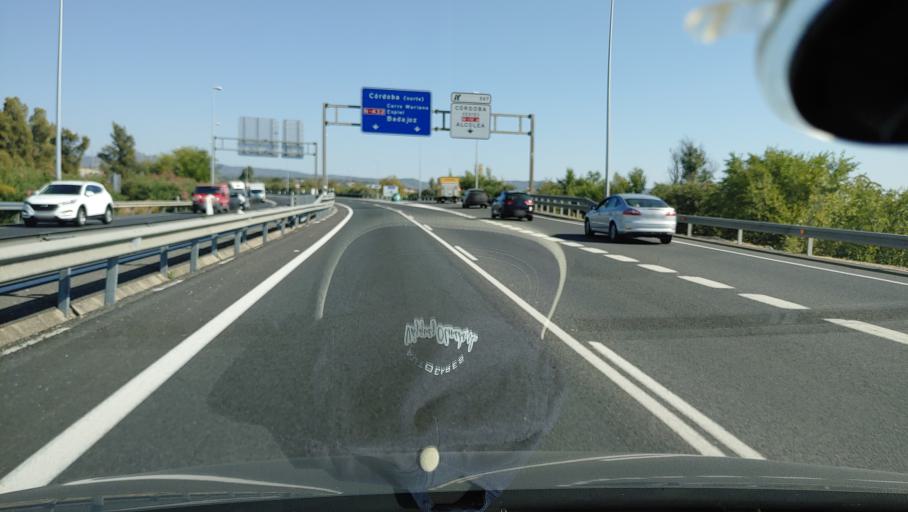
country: ES
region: Andalusia
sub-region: Province of Cordoba
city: Cordoba
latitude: 37.8918
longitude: -4.7455
